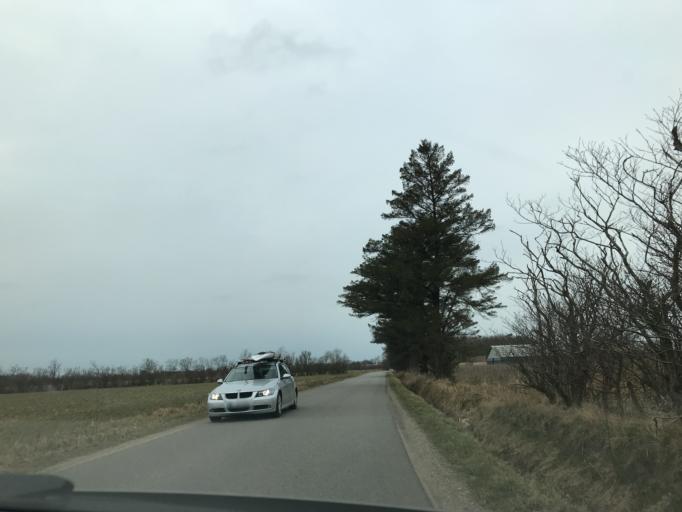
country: DK
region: South Denmark
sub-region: Varde Kommune
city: Oksbol
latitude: 55.8069
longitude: 8.3107
